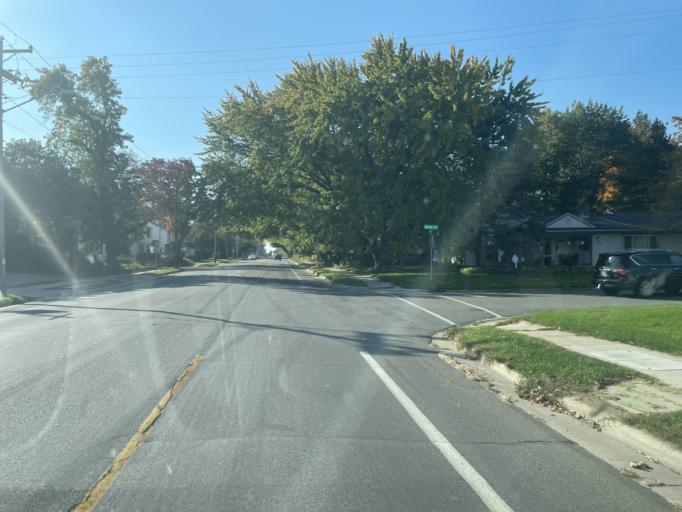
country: US
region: Wisconsin
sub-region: Dane County
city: Maple Bluff
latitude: 43.1210
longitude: -89.3638
